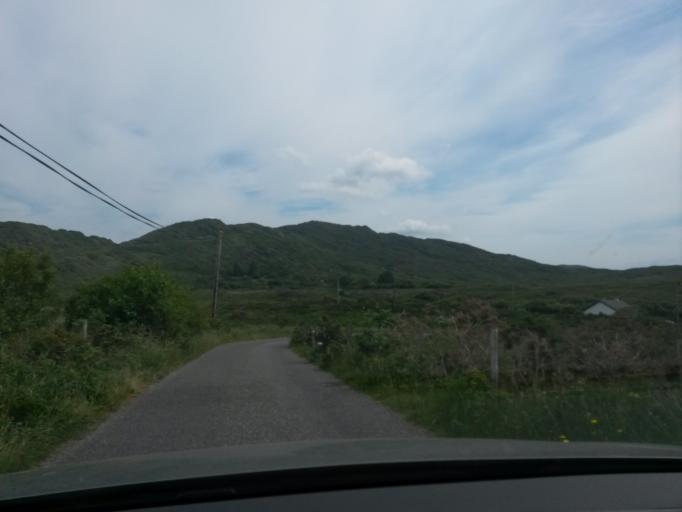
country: IE
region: Munster
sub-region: Ciarrai
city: Cahersiveen
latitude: 51.8087
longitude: -9.9755
